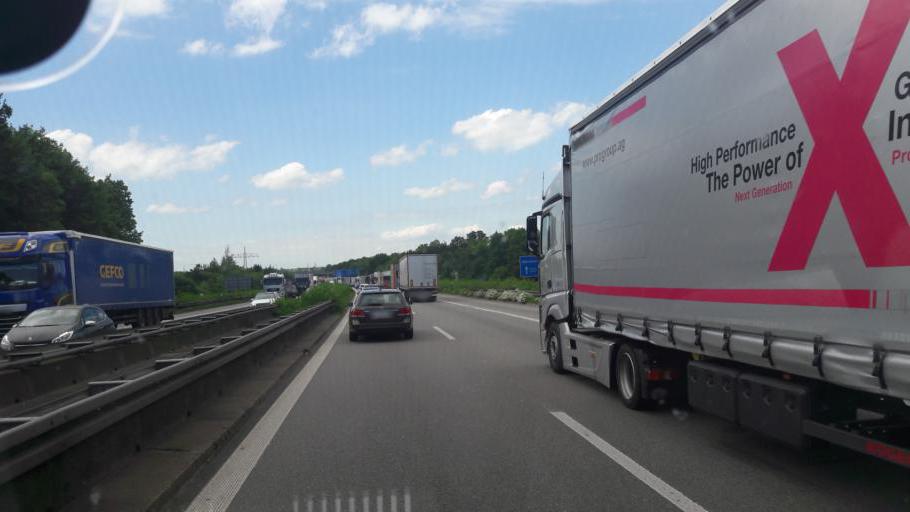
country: DE
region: Baden-Wuerttemberg
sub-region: Regierungsbezirk Stuttgart
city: Neckarsulm
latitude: 49.1806
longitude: 9.2299
